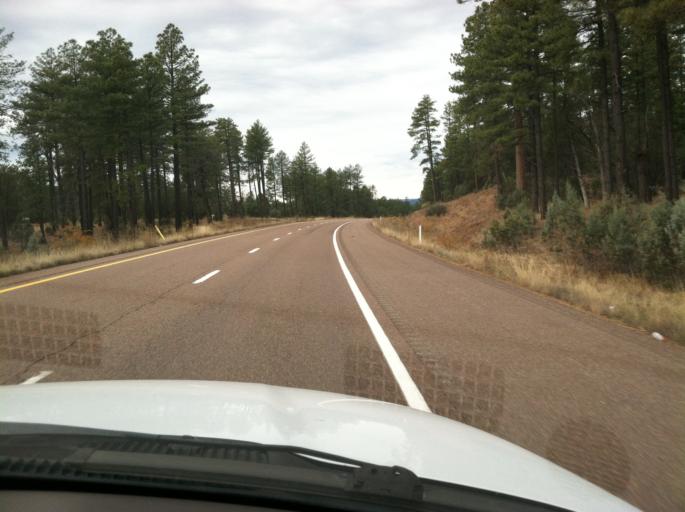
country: US
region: Arizona
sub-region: Gila County
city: Star Valley
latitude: 34.2946
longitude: -110.9783
